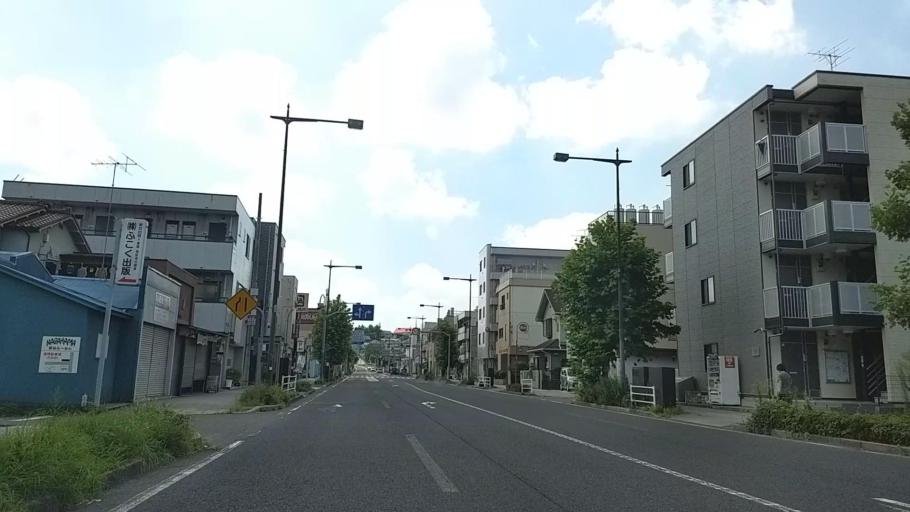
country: JP
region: Tokyo
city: Hachioji
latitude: 35.6533
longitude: 139.3330
